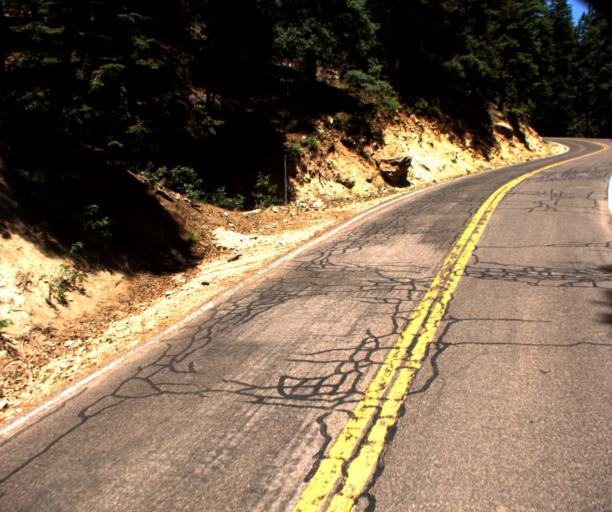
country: US
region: Arizona
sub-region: Graham County
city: Swift Trail Junction
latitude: 32.6270
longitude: -109.8278
